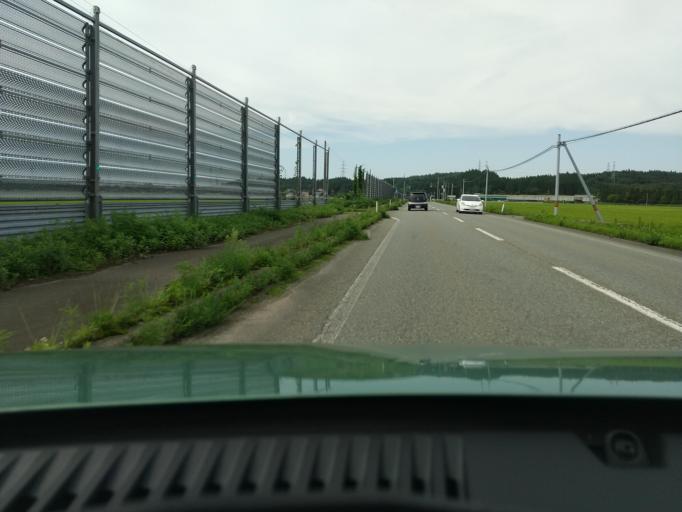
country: JP
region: Akita
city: Akita Shi
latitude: 39.7986
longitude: 140.0951
